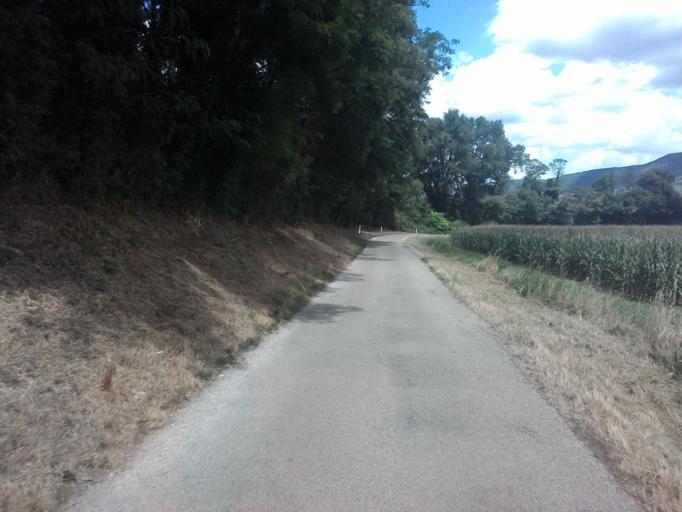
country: FR
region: Rhone-Alpes
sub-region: Departement de l'Ain
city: Lagnieu
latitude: 45.8807
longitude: 5.3478
